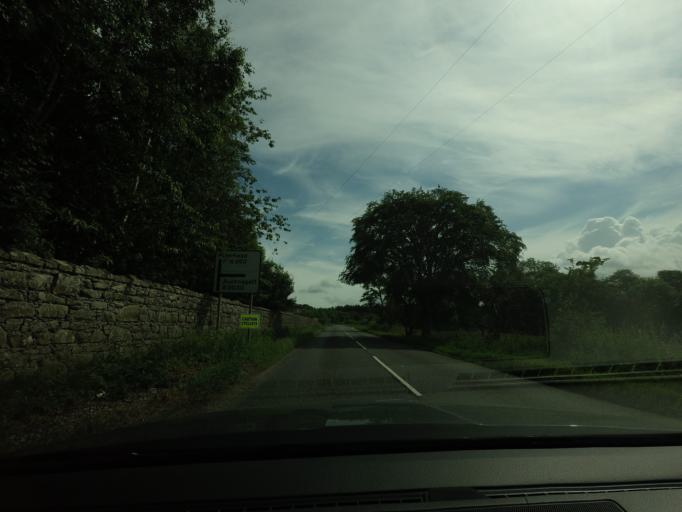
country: GB
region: Scotland
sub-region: Aberdeenshire
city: Mintlaw
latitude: 57.5248
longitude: -2.0394
